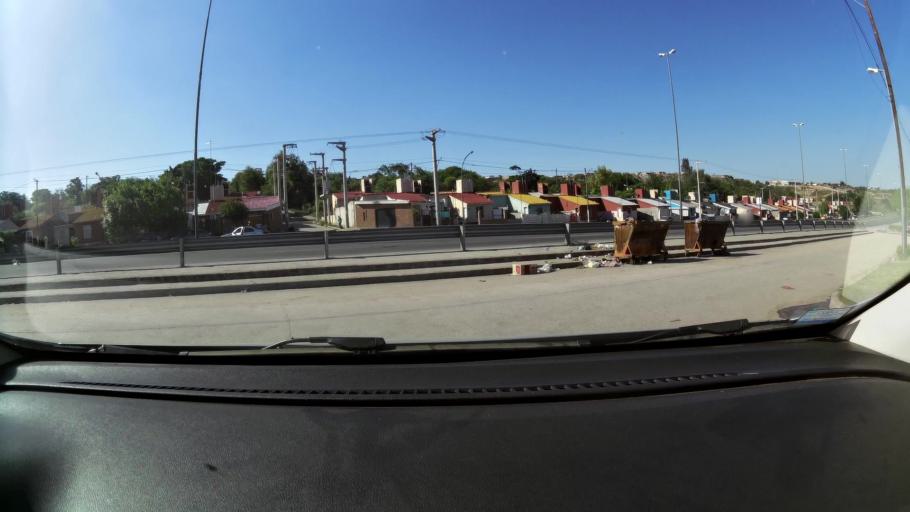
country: AR
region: Cordoba
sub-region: Departamento de Capital
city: Cordoba
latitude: -31.4016
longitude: -64.1495
